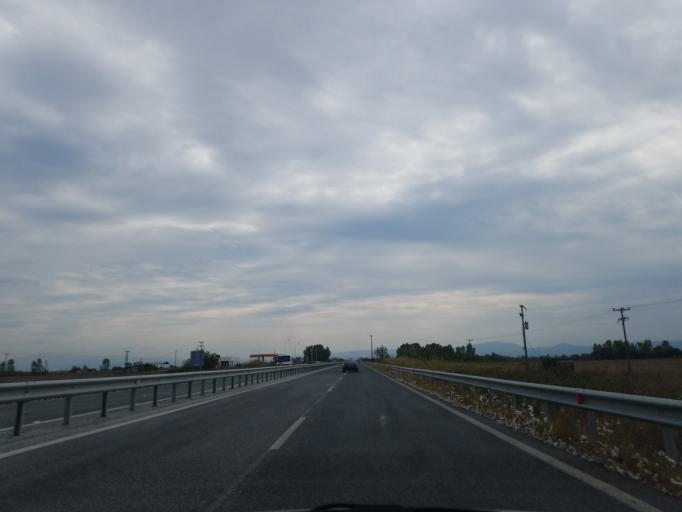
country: GR
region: Thessaly
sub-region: Nomos Kardhitsas
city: Sofades
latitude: 39.3174
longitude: 22.1142
